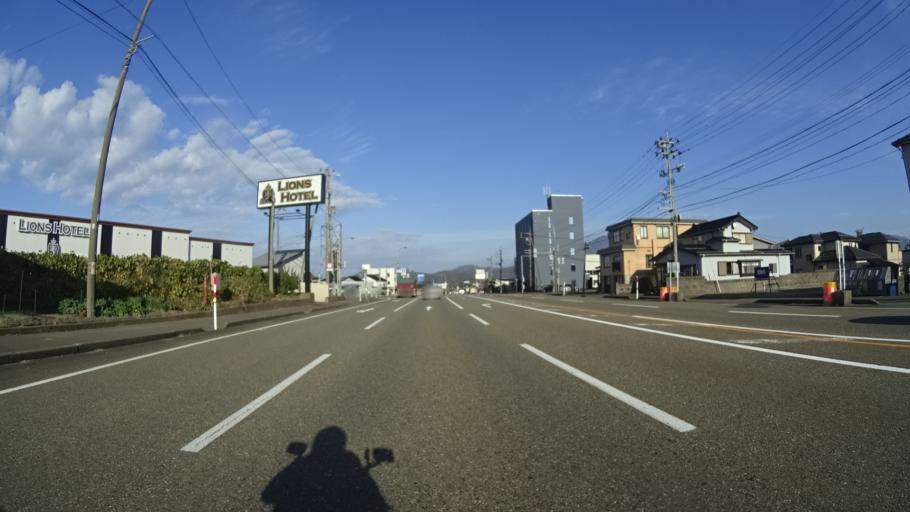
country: JP
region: Niigata
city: Joetsu
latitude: 37.2658
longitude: 138.3801
